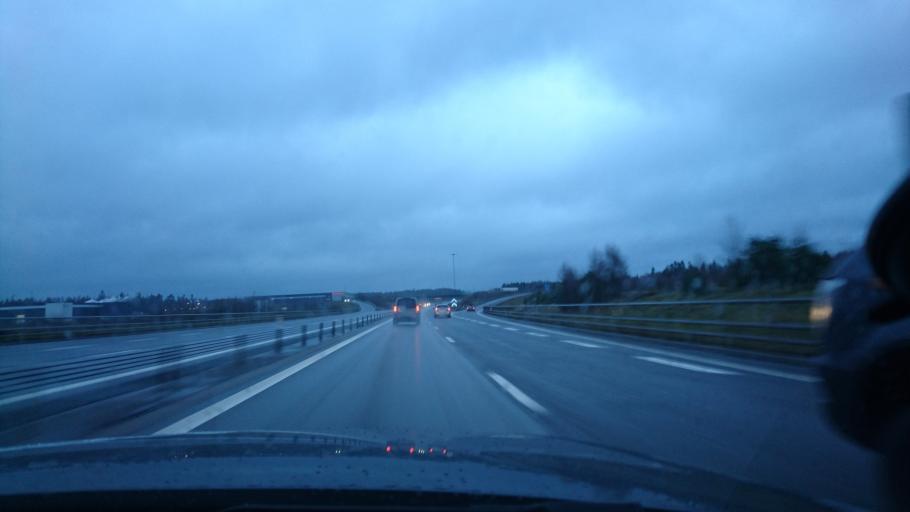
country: SE
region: Kronoberg
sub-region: Markaryds Kommun
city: Markaryd
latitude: 56.4649
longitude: 13.6301
